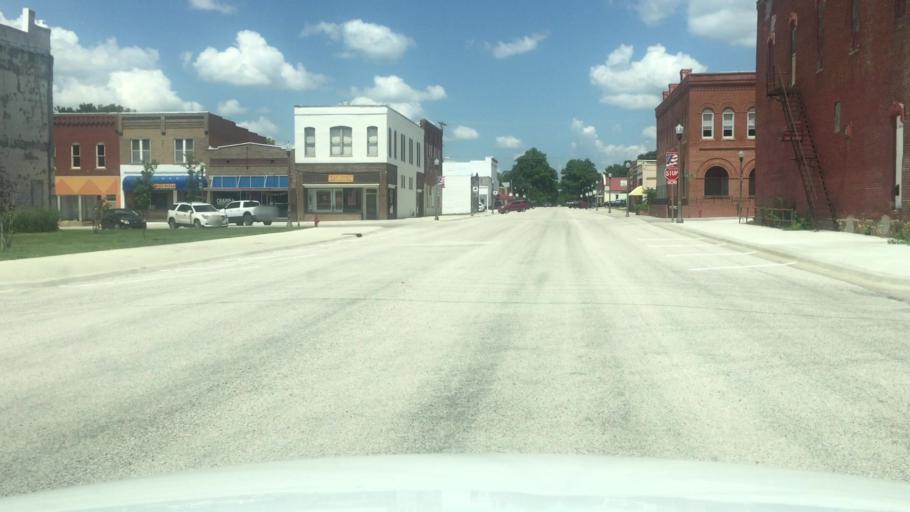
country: US
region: Kansas
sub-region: Brown County
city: Horton
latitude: 39.6595
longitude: -95.5274
